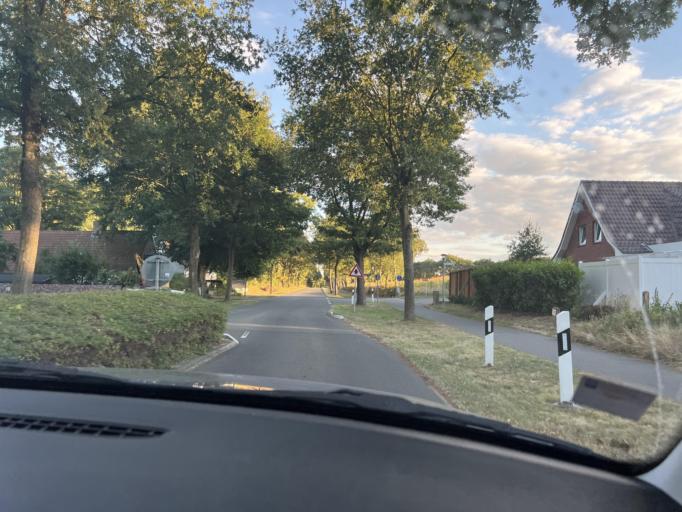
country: DE
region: Schleswig-Holstein
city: Weddingstedt
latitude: 54.2207
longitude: 9.0938
